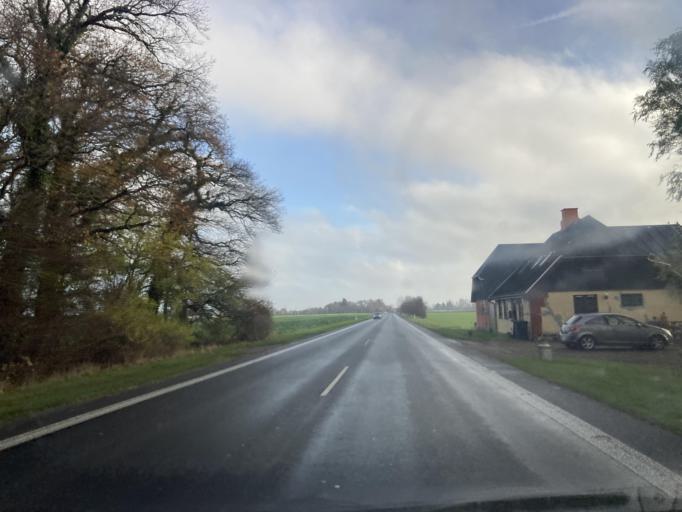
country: DK
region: Zealand
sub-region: Lolland Kommune
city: Maribo
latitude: 54.8139
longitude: 11.3955
